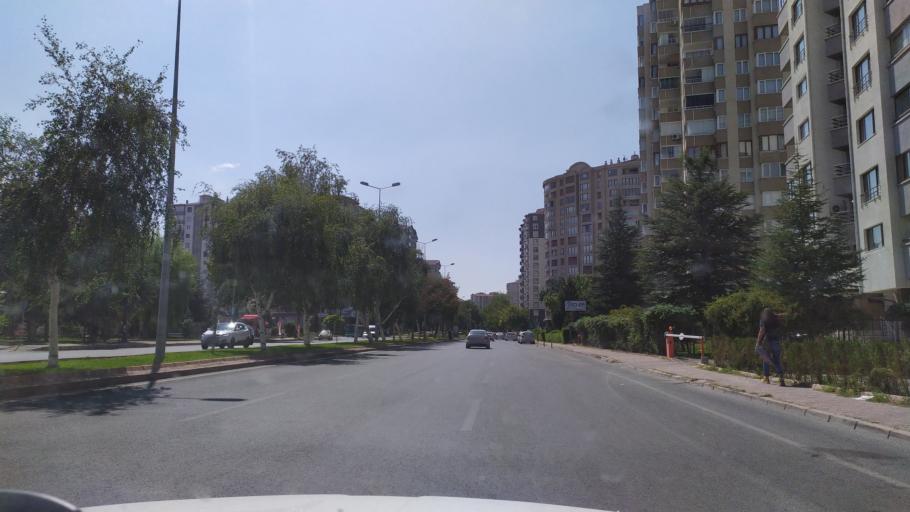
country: TR
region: Kayseri
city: Kayseri
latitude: 38.7261
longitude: 35.5219
